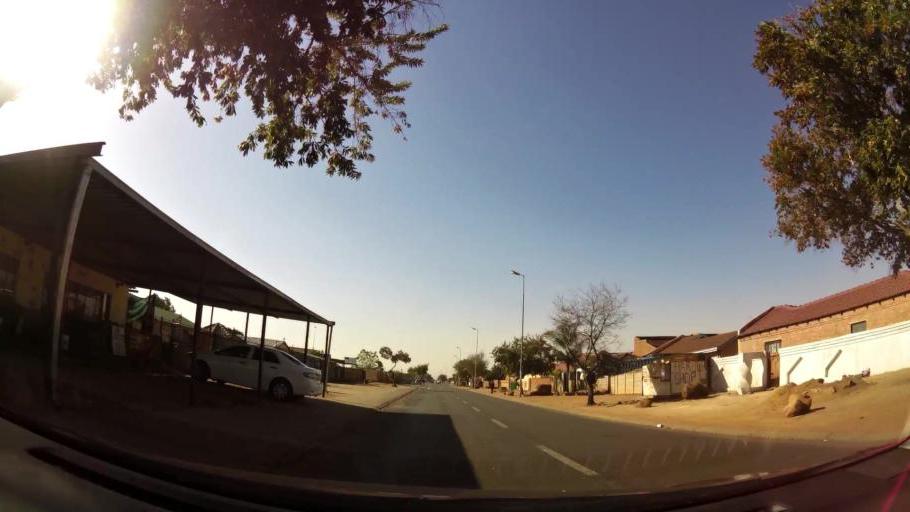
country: ZA
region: Gauteng
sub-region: City of Tshwane Metropolitan Municipality
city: Mabopane
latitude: -25.5345
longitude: 28.1014
